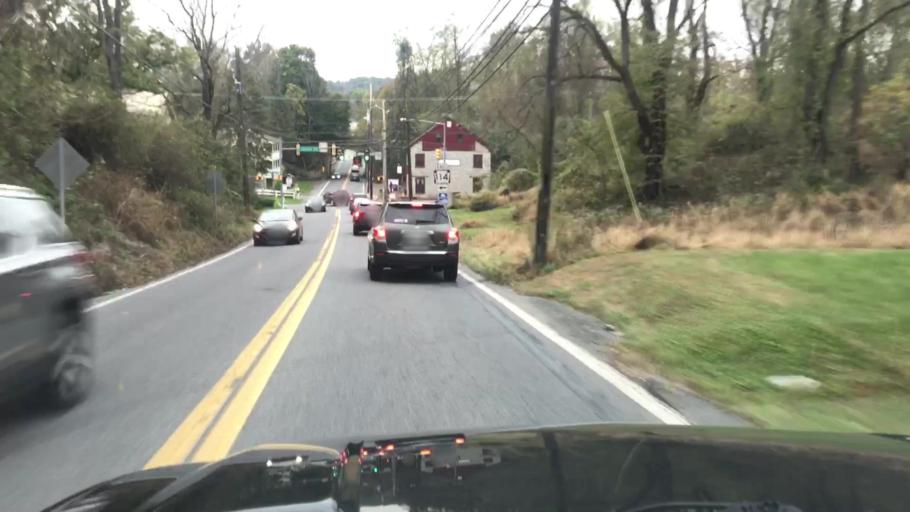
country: US
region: Pennsylvania
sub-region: Cumberland County
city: Mechanicsburg
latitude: 40.1671
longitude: -76.9786
